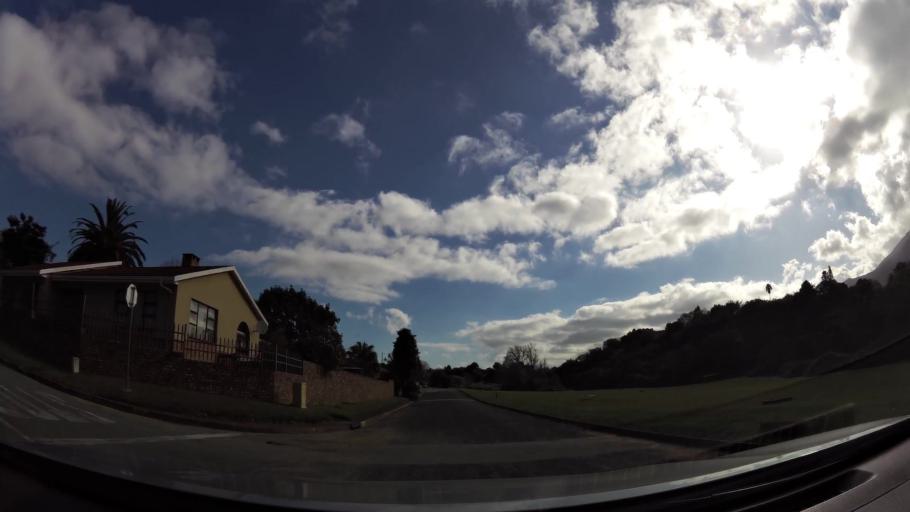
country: ZA
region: Western Cape
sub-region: Eden District Municipality
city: George
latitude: -33.9539
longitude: 22.4764
